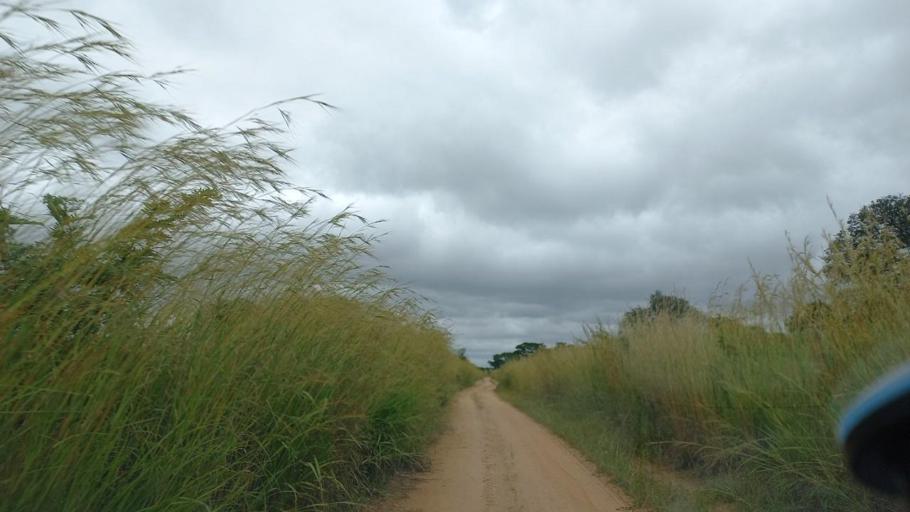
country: ZM
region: Lusaka
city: Lusaka
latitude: -15.1330
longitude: 28.3690
